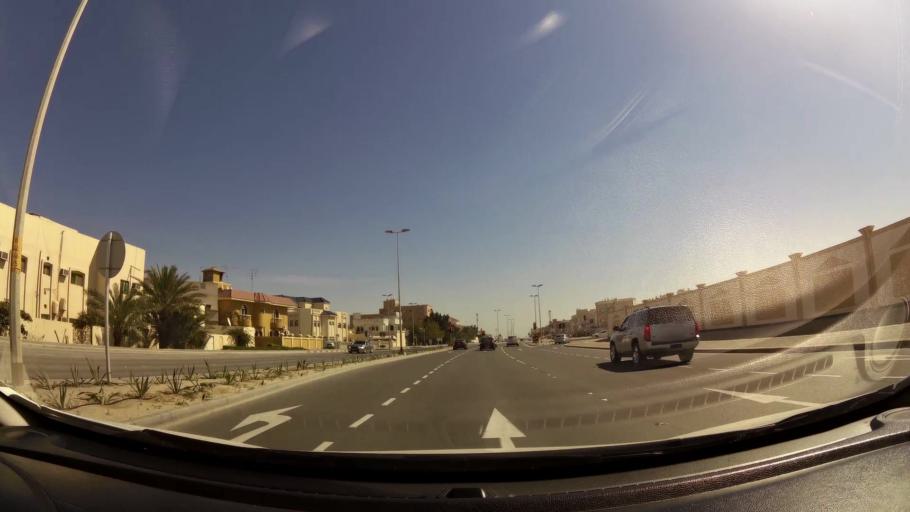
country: BH
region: Muharraq
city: Al Hadd
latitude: 26.2542
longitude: 50.6395
